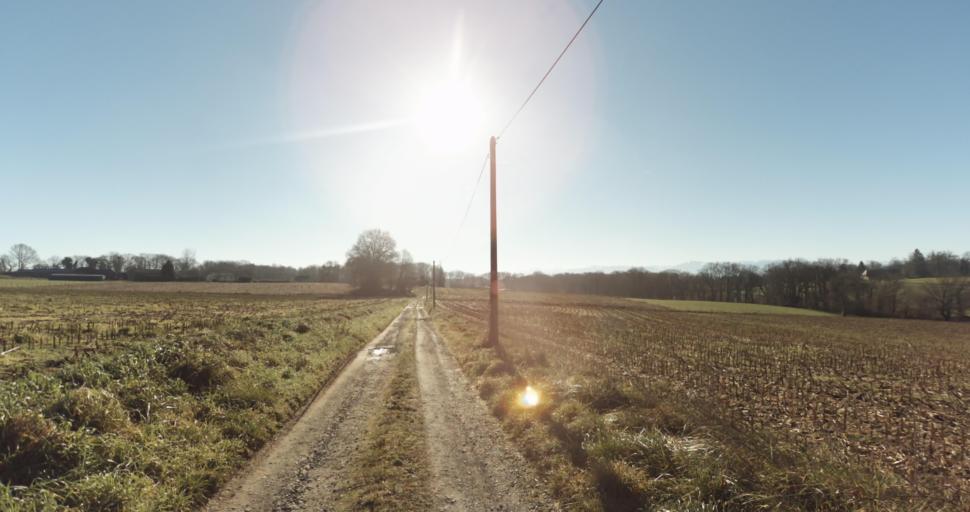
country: FR
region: Aquitaine
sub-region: Departement des Pyrenees-Atlantiques
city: Morlaas
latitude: 43.3457
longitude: -0.2467
